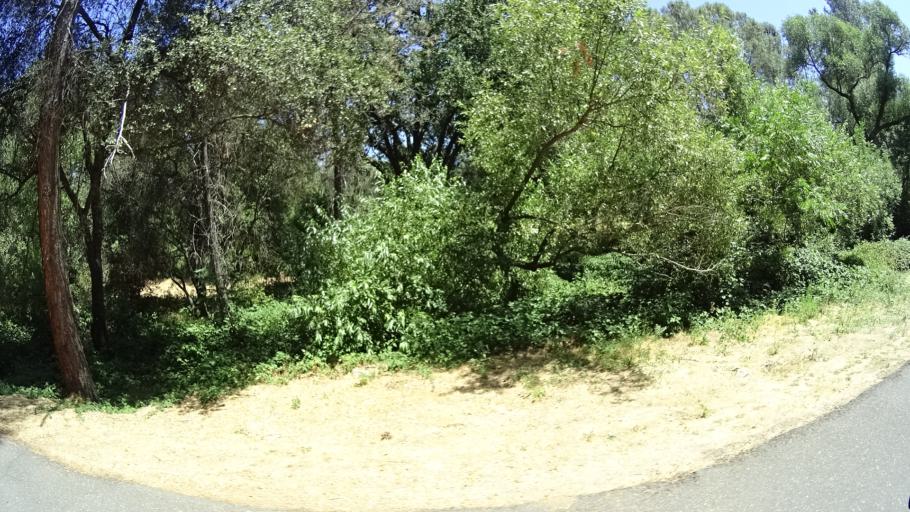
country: US
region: California
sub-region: Calaveras County
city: Angels Camp
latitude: 38.0934
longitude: -120.5040
